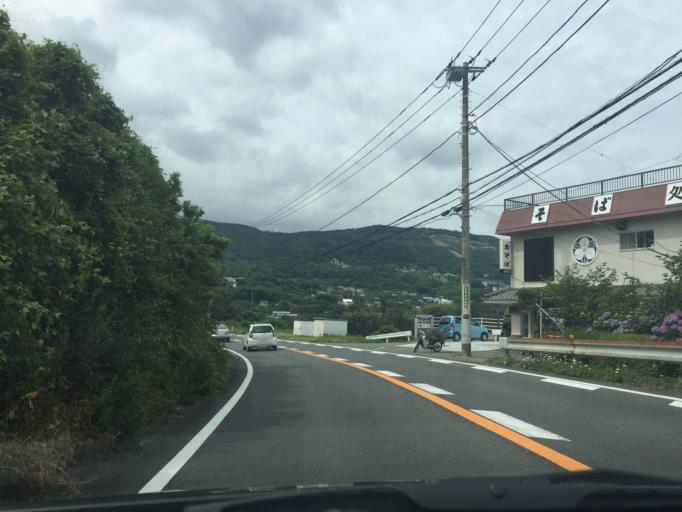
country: JP
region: Shizuoka
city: Shimoda
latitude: 34.7708
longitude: 139.0385
